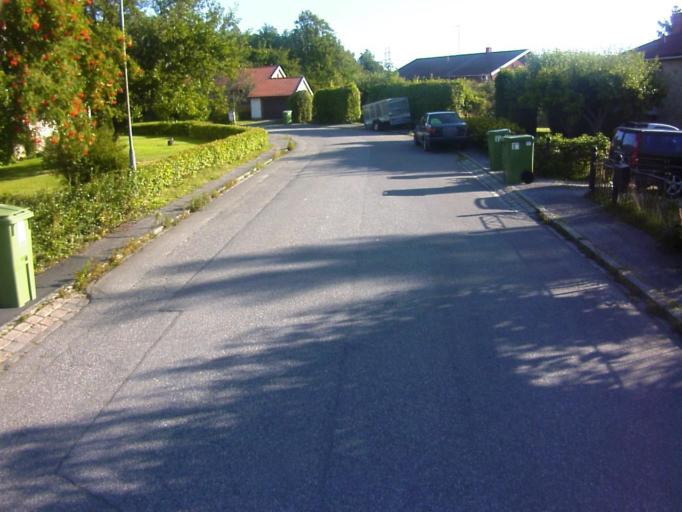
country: SE
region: Soedermanland
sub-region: Eskilstuna Kommun
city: Eskilstuna
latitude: 59.3808
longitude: 16.5380
